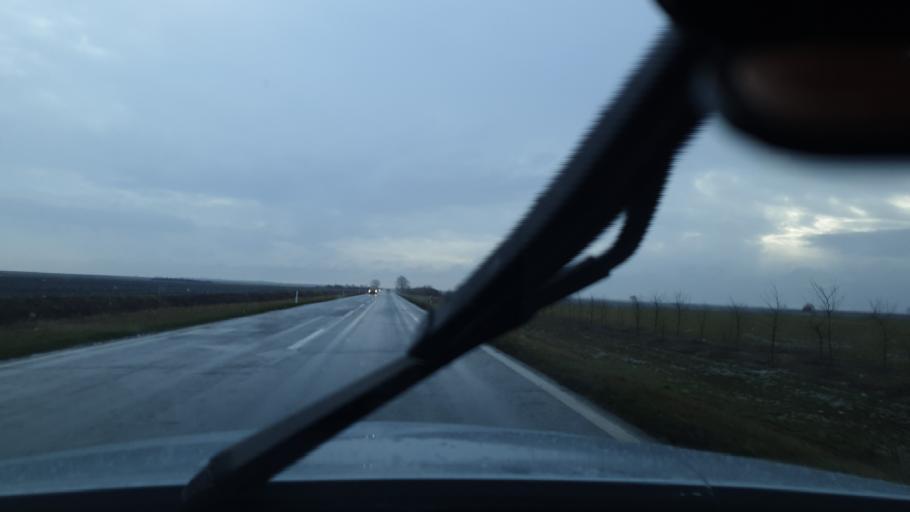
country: RS
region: Autonomna Pokrajina Vojvodina
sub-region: Juznobanatski Okrug
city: Pancevo
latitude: 44.8417
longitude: 20.7966
